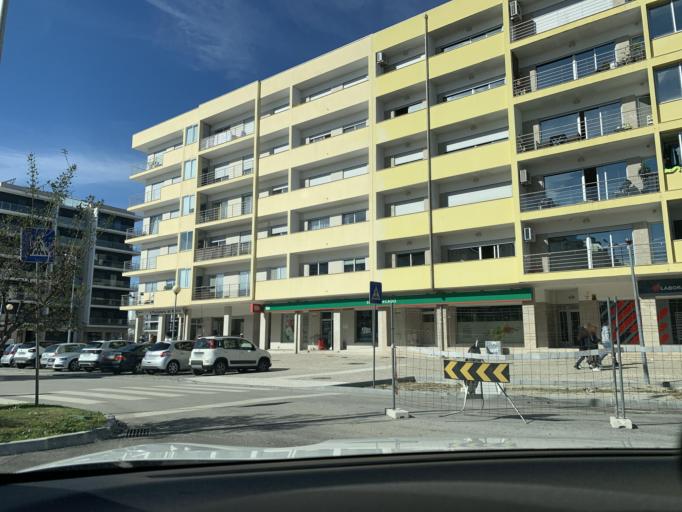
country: PT
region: Viseu
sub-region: Viseu
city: Viseu
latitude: 40.6472
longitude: -7.9143
